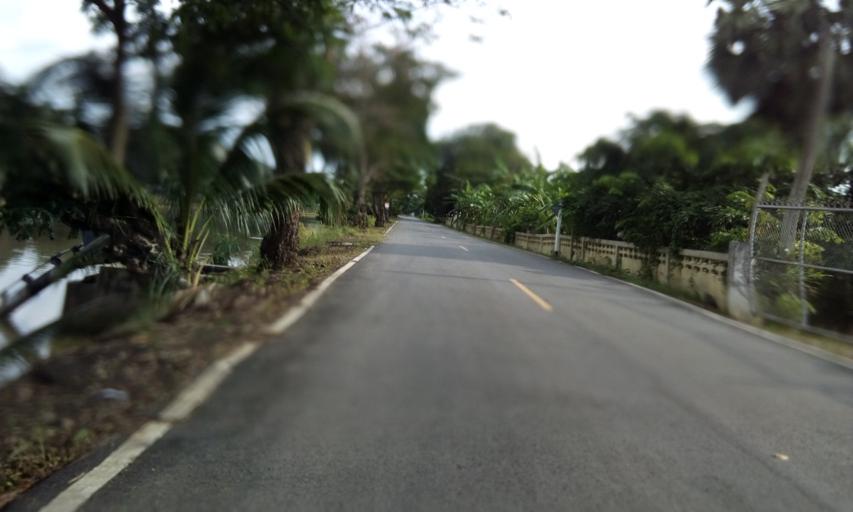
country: TH
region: Pathum Thani
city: Nong Suea
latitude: 14.1498
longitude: 100.8232
